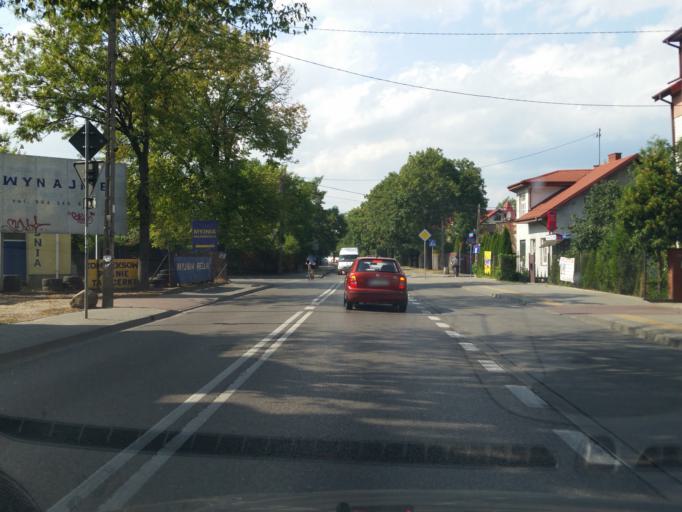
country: PL
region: Masovian Voivodeship
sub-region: Warszawa
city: Ursus
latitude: 52.1976
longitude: 20.8792
